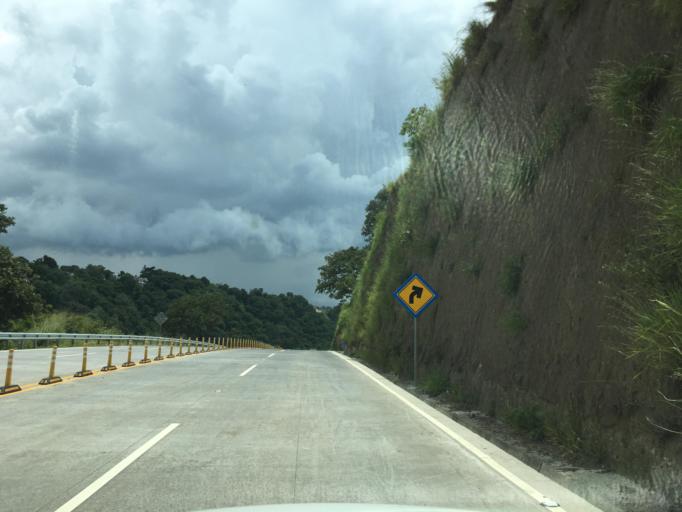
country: GT
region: Guatemala
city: Santa Catarina Pinula
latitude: 14.5480
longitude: -90.5321
